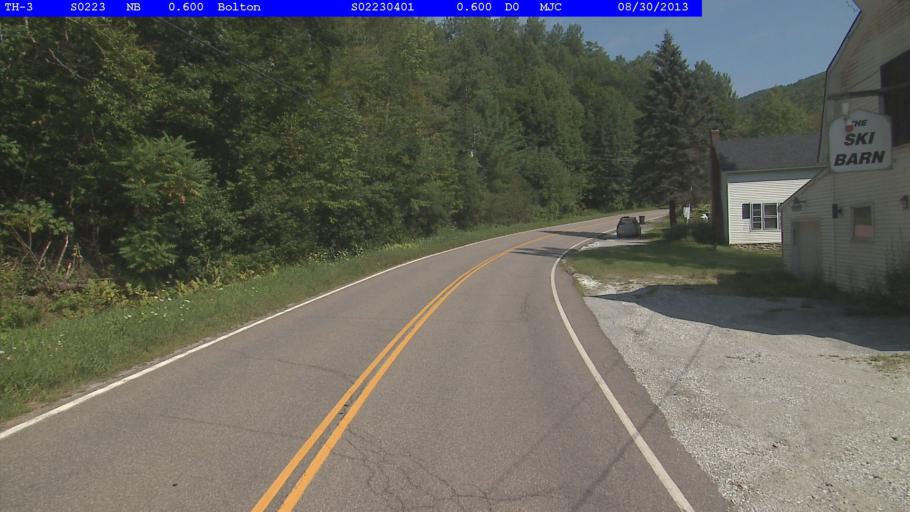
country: US
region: Vermont
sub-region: Washington County
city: Waterbury
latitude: 44.3798
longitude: -72.8763
